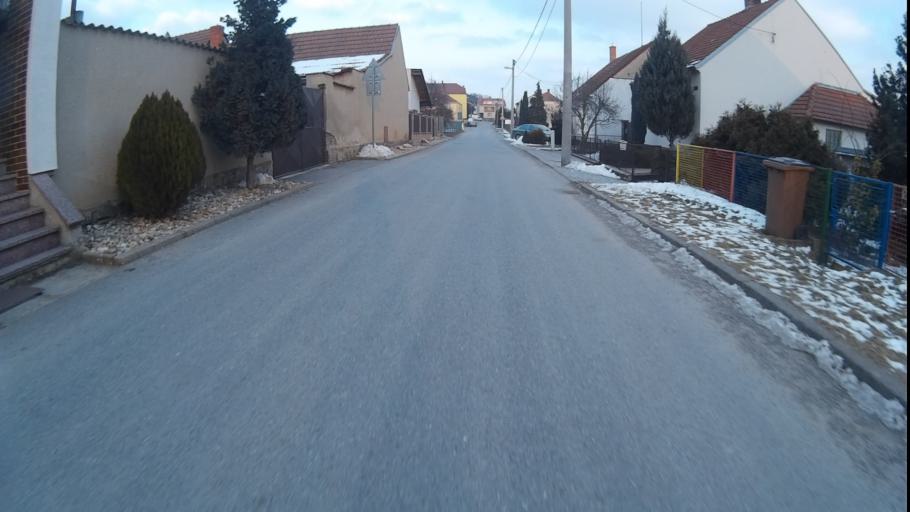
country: CZ
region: South Moravian
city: Vinicne Sumice
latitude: 49.2133
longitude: 16.8193
